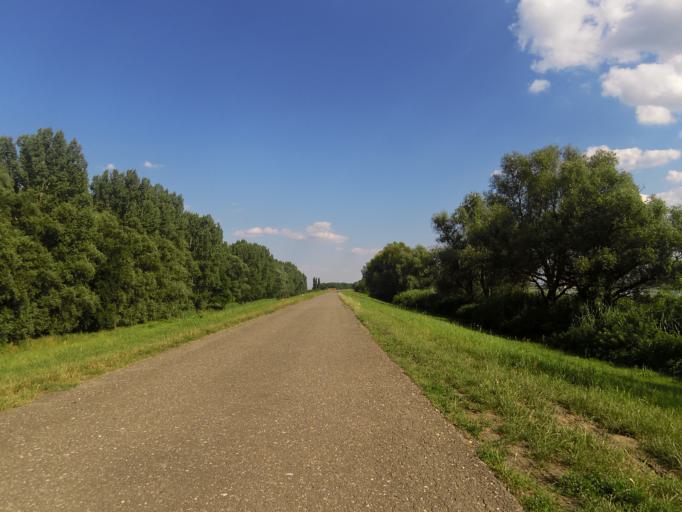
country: HU
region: Jasz-Nagykun-Szolnok
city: Abadszalok
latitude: 47.5025
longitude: 20.5991
